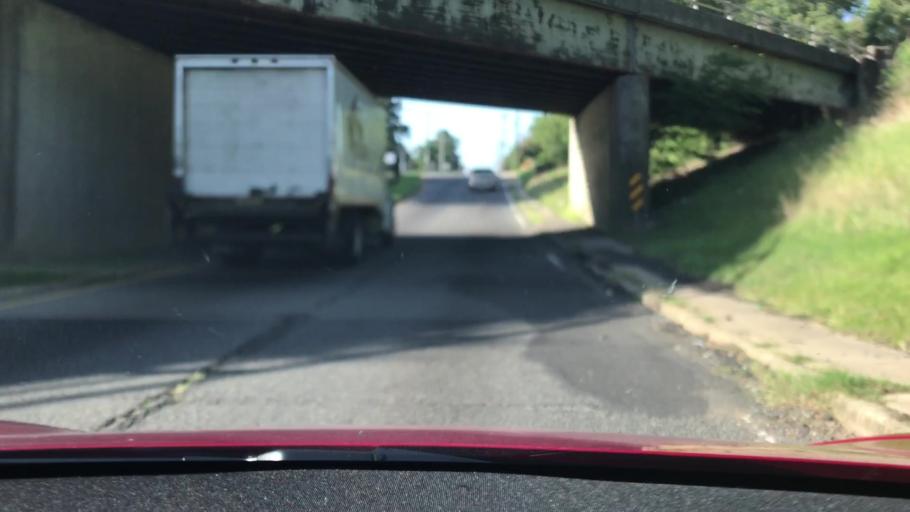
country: US
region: Louisiana
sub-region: Caddo Parish
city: Shreveport
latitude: 32.4693
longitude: -93.7802
